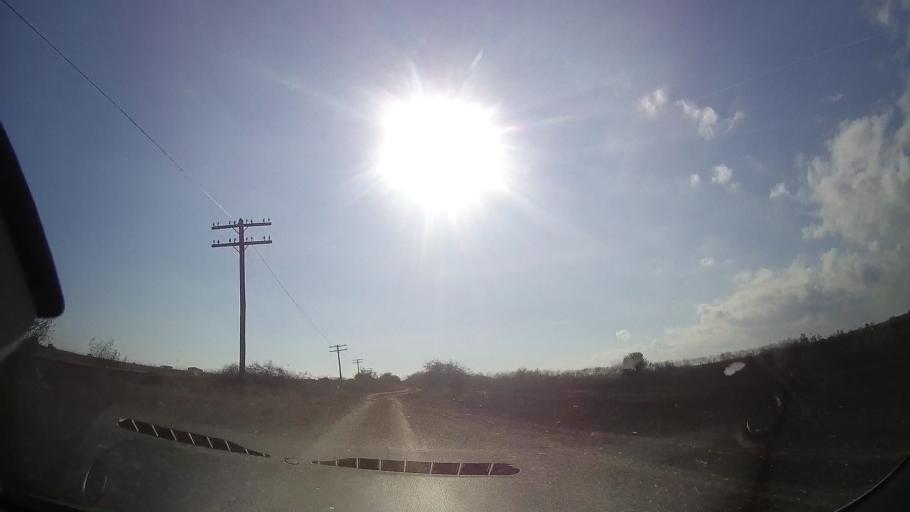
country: RO
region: Constanta
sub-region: Comuna Tuzla
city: Tuzla
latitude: 43.9762
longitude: 28.6441
